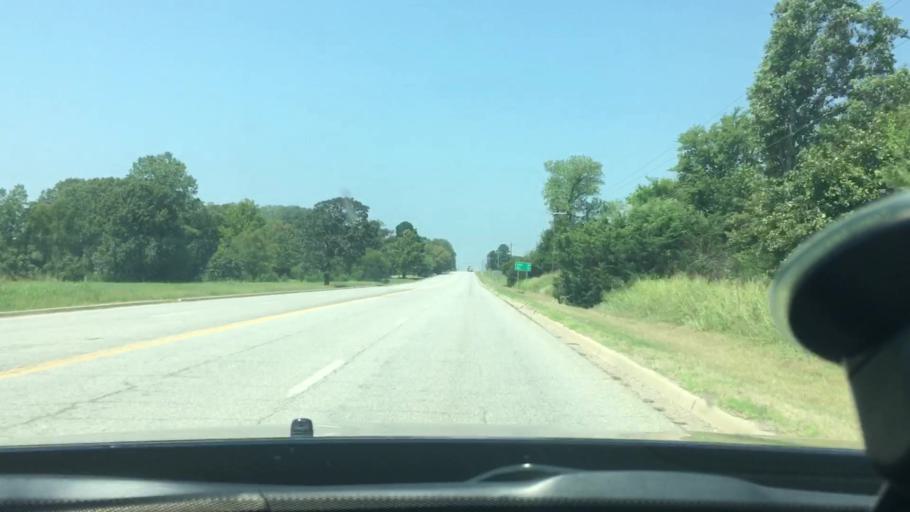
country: US
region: Oklahoma
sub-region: Atoka County
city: Atoka
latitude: 34.3026
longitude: -95.9974
